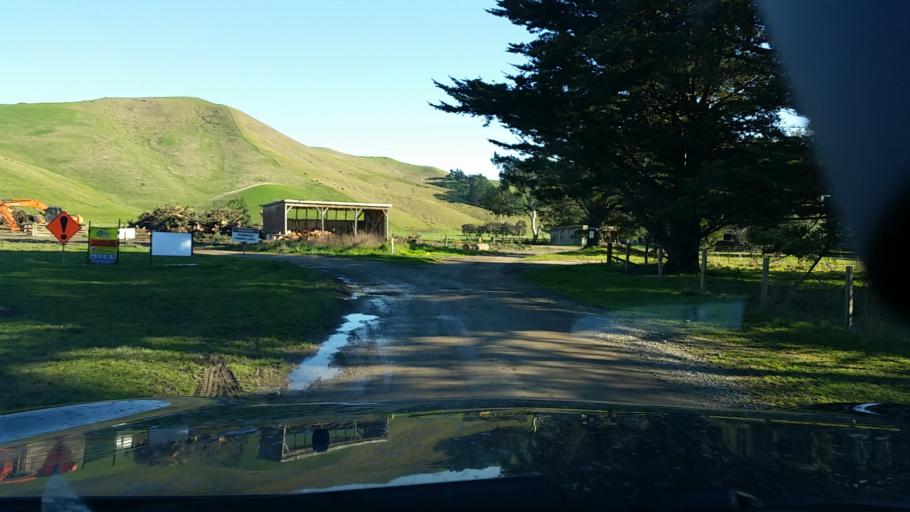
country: NZ
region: Marlborough
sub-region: Marlborough District
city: Blenheim
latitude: -41.5617
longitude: 173.9251
